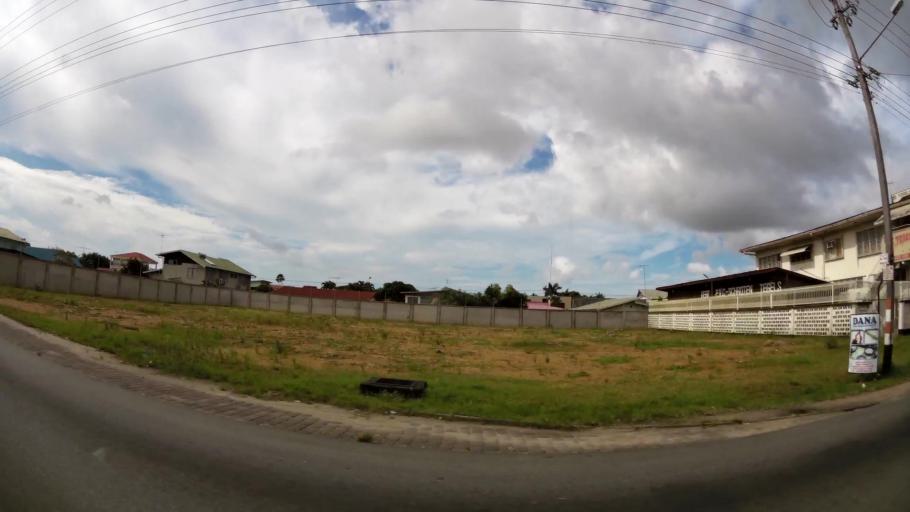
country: SR
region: Paramaribo
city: Paramaribo
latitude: 5.8403
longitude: -55.1855
